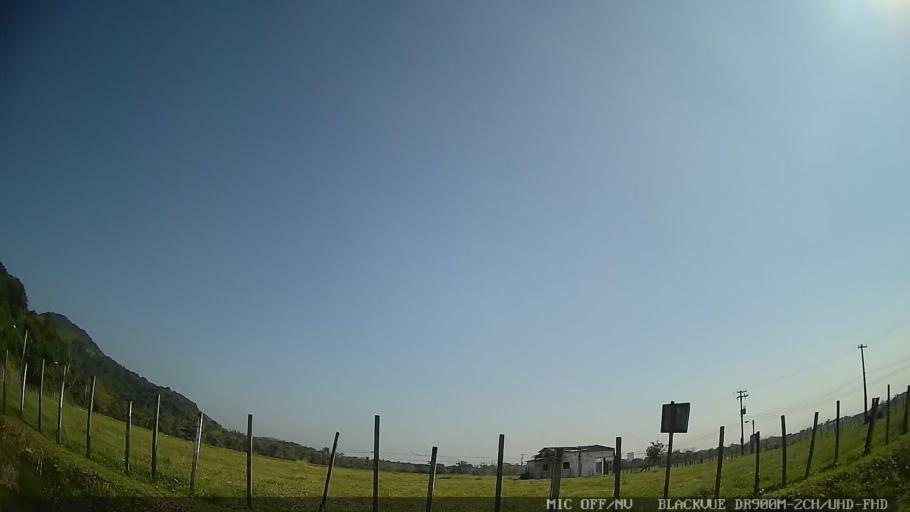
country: BR
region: Sao Paulo
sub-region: Guaruja
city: Guaruja
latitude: -24.0078
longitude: -46.2773
